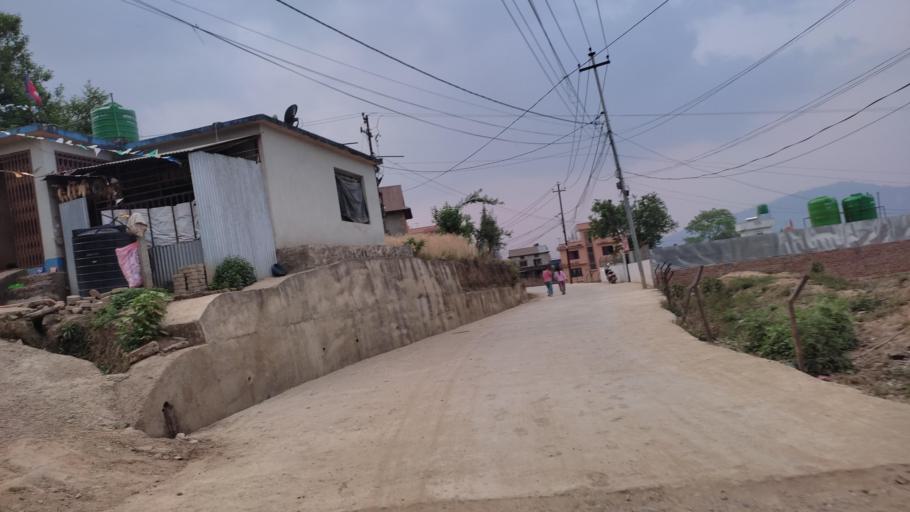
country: NP
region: Central Region
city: Kirtipur
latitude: 27.6690
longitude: 85.2459
